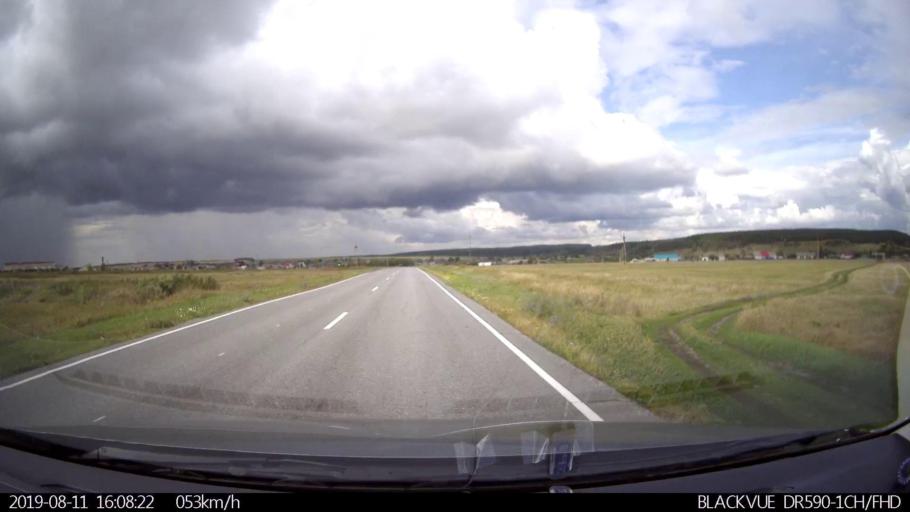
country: RU
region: Ulyanovsk
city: Ignatovka
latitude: 53.9841
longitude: 47.6477
